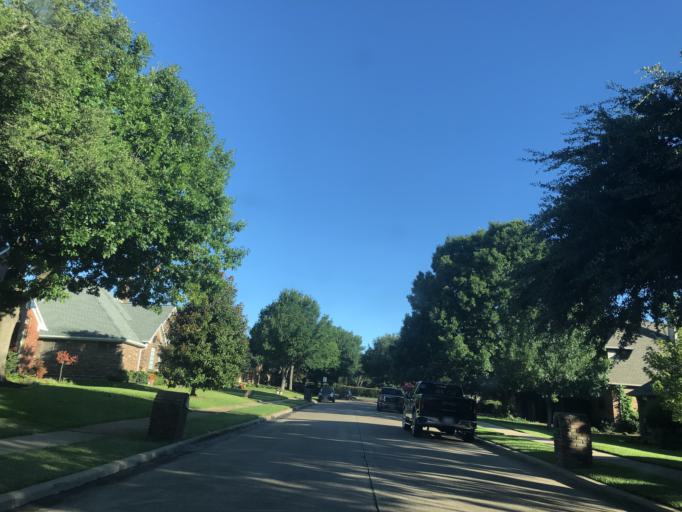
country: US
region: Texas
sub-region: Dallas County
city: Garland
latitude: 32.8367
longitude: -96.6439
